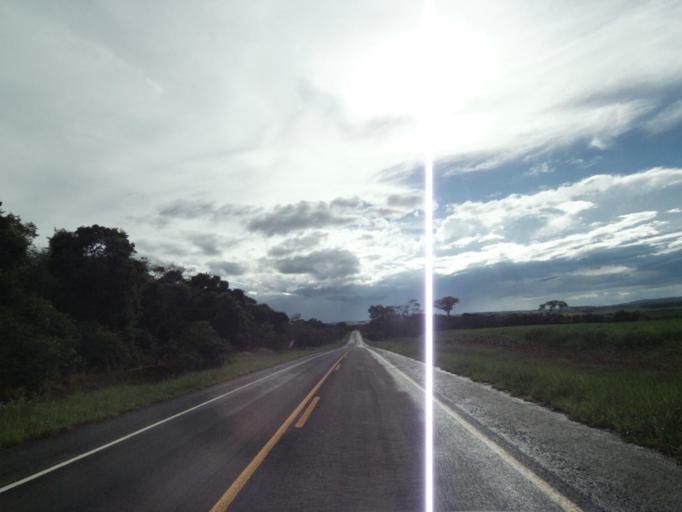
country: BR
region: Goias
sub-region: Itaberai
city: Itaberai
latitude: -15.9095
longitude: -49.5762
